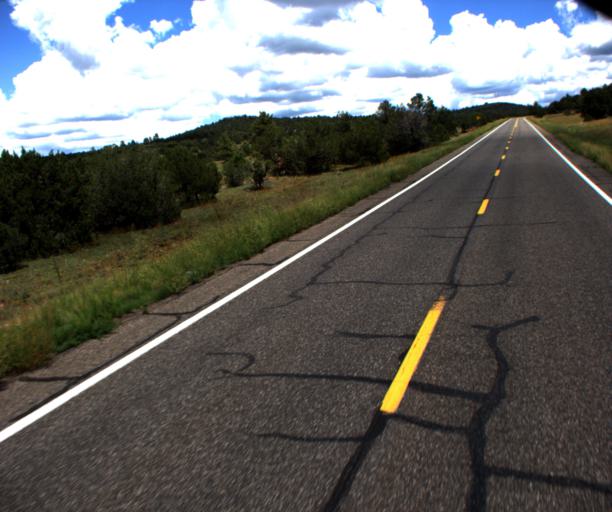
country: US
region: Arizona
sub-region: Gila County
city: Pine
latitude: 34.5077
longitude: -111.5633
